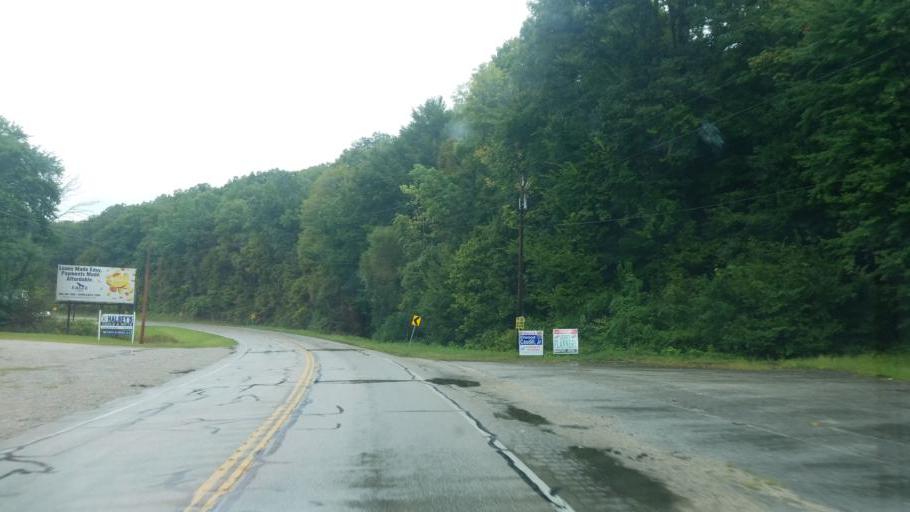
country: US
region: Kentucky
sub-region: Rowan County
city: Morehead
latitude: 38.1536
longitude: -83.4941
